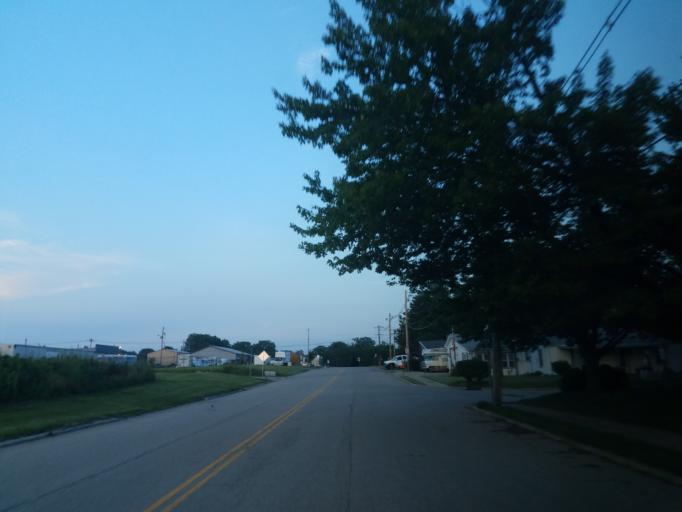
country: US
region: Illinois
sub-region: McLean County
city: Bloomington
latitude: 40.4417
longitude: -88.9932
